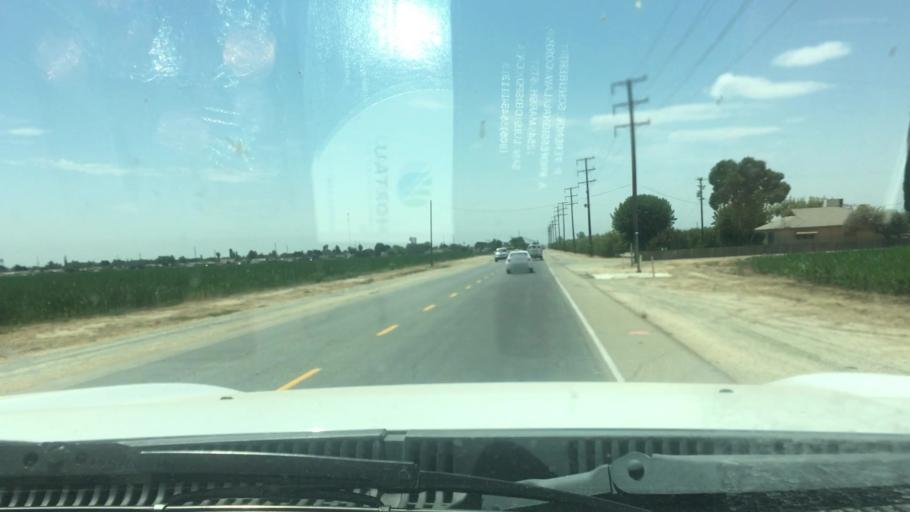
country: US
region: California
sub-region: Tulare County
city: Tipton
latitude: 36.0657
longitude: -119.2949
